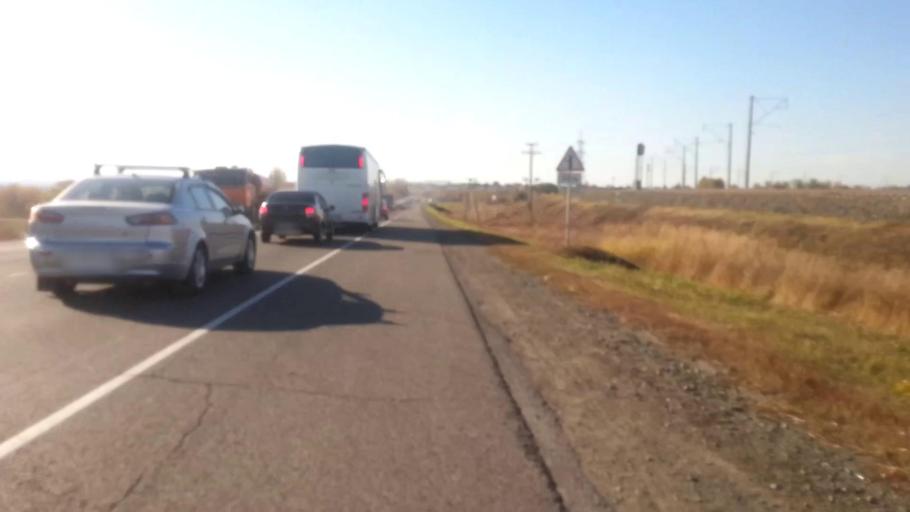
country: RU
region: Altai Krai
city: Novoaltaysk
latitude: 53.3737
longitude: 83.9424
